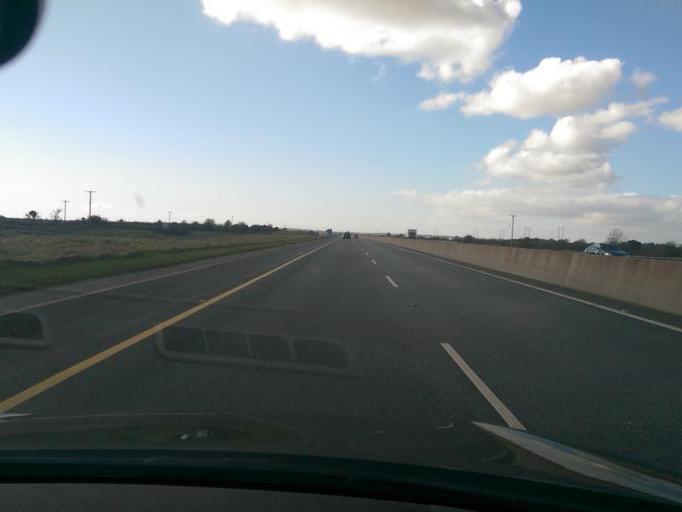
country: IE
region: Connaught
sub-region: County Galway
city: Oranmore
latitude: 53.2997
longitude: -8.8763
